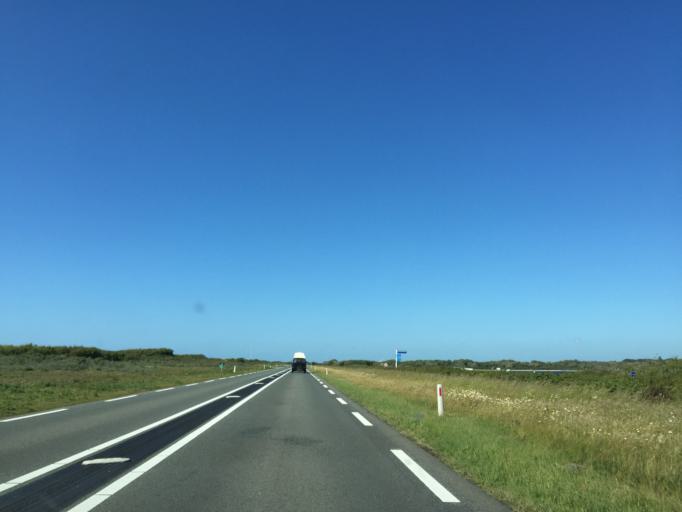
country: NL
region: Zeeland
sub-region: Schouwen-Duiveland
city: Scharendijke
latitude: 51.7749
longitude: 3.8646
